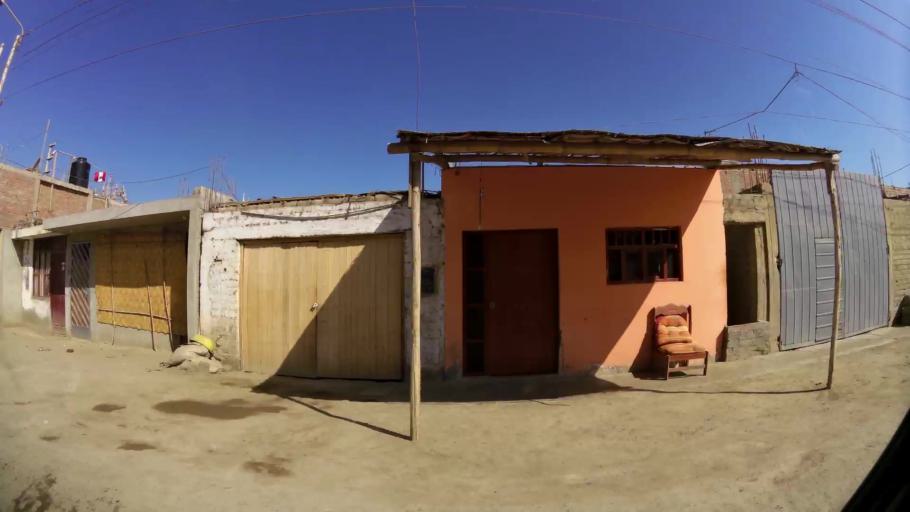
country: PE
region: Ancash
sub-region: Provincia de Huarmey
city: Huarmey
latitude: -10.0630
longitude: -78.1537
